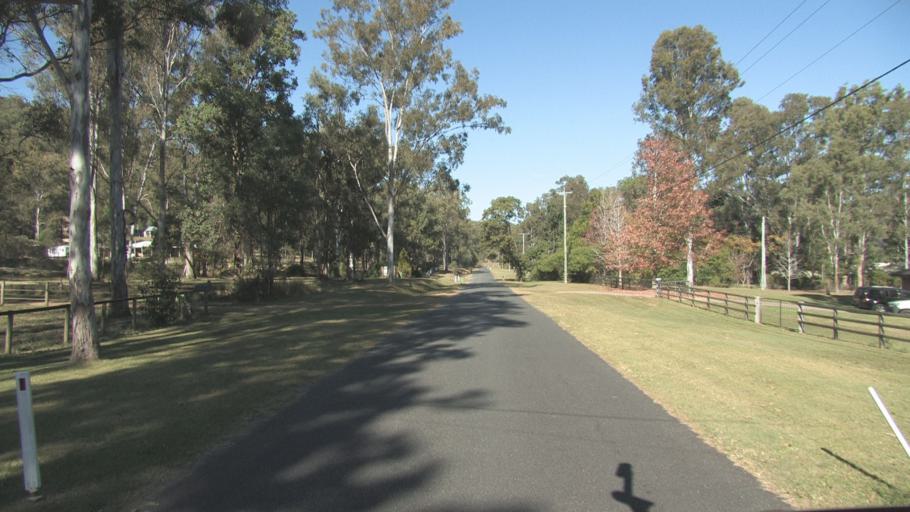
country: AU
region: Queensland
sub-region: Logan
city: Windaroo
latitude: -27.7815
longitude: 153.1480
